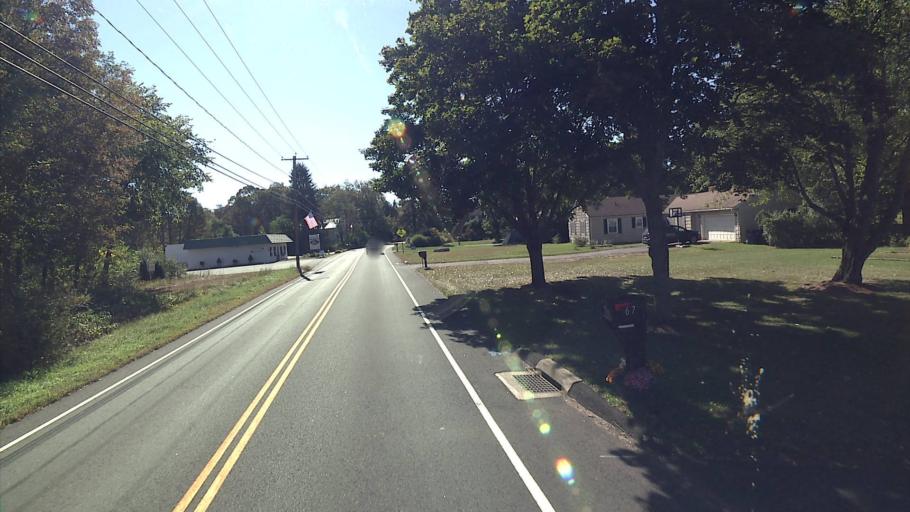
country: US
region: Connecticut
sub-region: Tolland County
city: Somers
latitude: 41.9903
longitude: -72.4481
